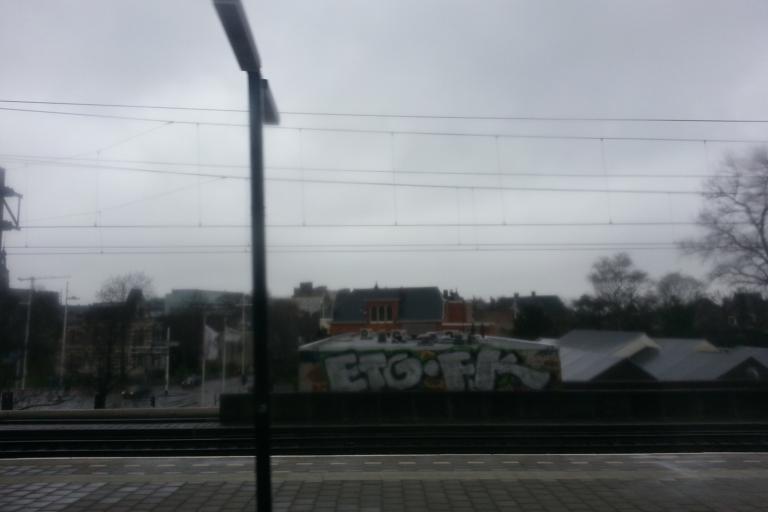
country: NL
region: South Holland
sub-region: Gemeente Leiden
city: Leiden
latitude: 52.1675
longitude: 4.4835
